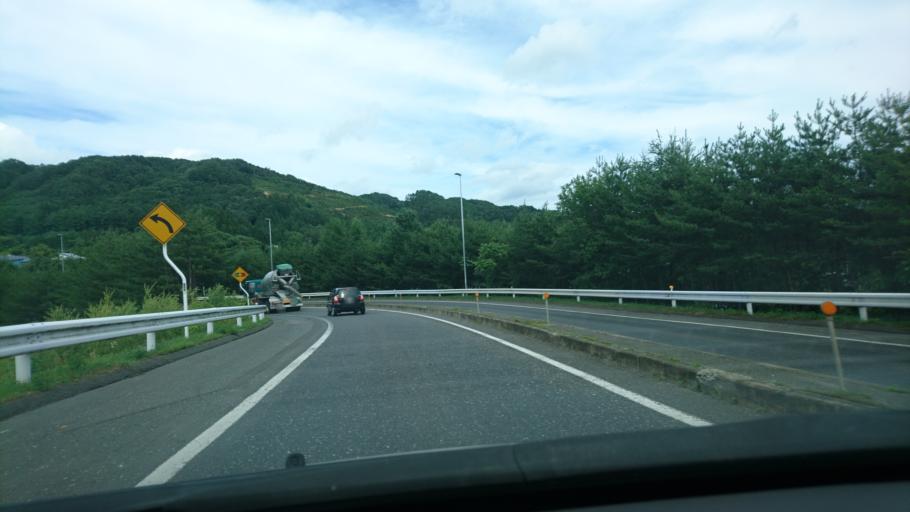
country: JP
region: Aomori
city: Hachinohe
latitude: 40.2217
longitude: 141.7832
